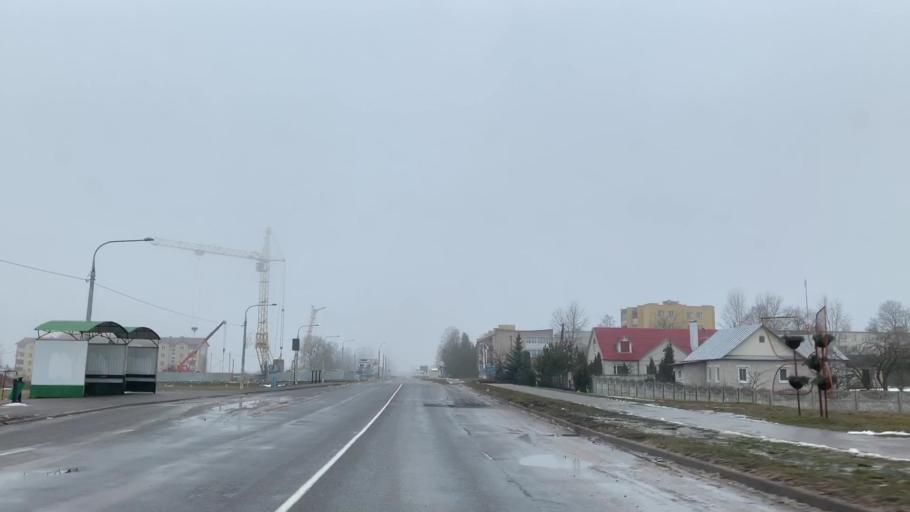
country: BY
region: Minsk
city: Nyasvizh
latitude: 53.2342
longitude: 26.6480
